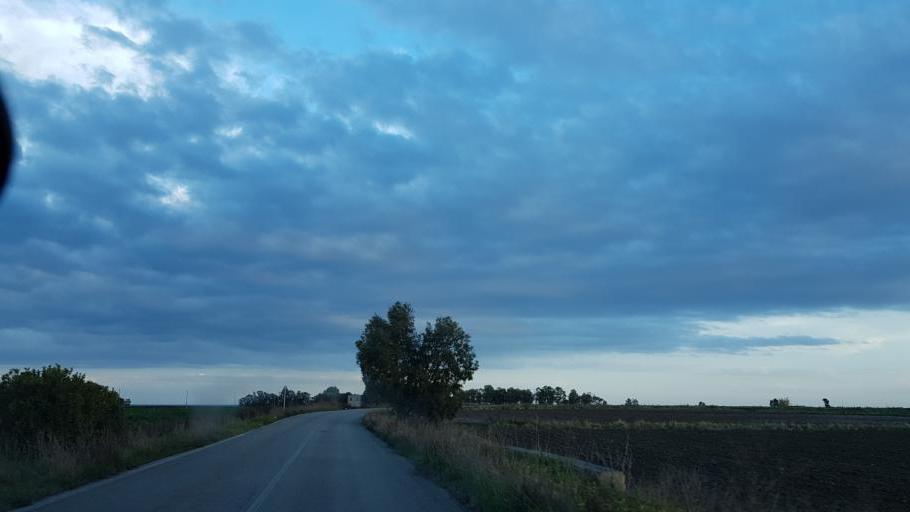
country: IT
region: Apulia
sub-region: Provincia di Brindisi
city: La Rosa
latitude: 40.5853
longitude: 18.0310
